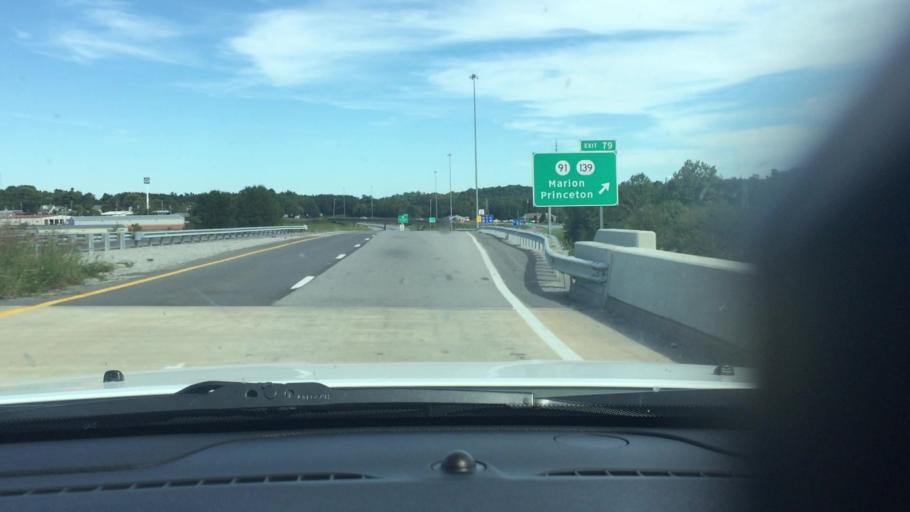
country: US
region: Kentucky
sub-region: Caldwell County
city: Princeton
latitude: 37.1213
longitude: -87.8991
